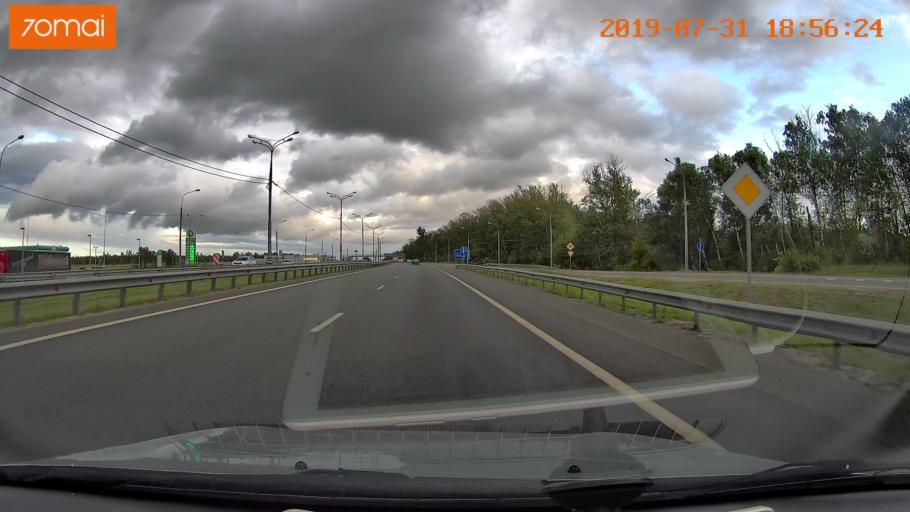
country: RU
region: Moskovskaya
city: Raduzhnyy
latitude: 55.1635
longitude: 38.6774
